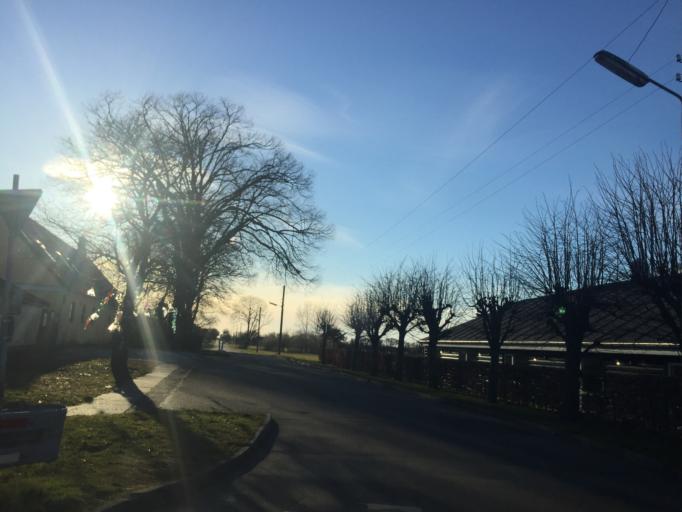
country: DK
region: Capital Region
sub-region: Dragor Kommune
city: Dragor
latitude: 55.6011
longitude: 12.6588
